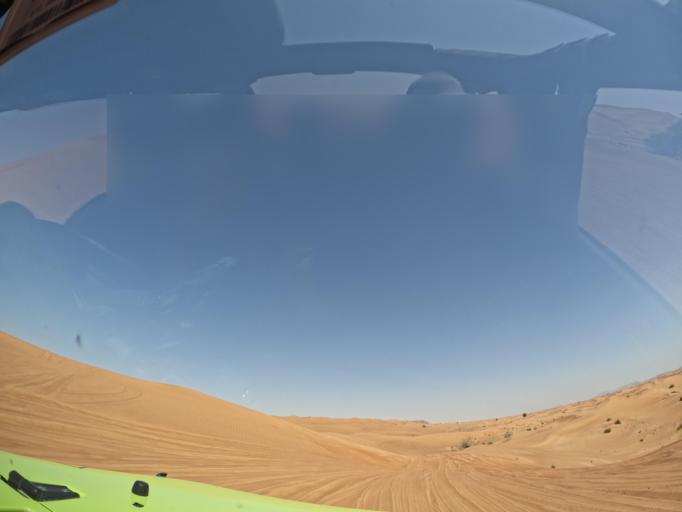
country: AE
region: Ash Shariqah
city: Adh Dhayd
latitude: 24.9913
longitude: 55.7238
